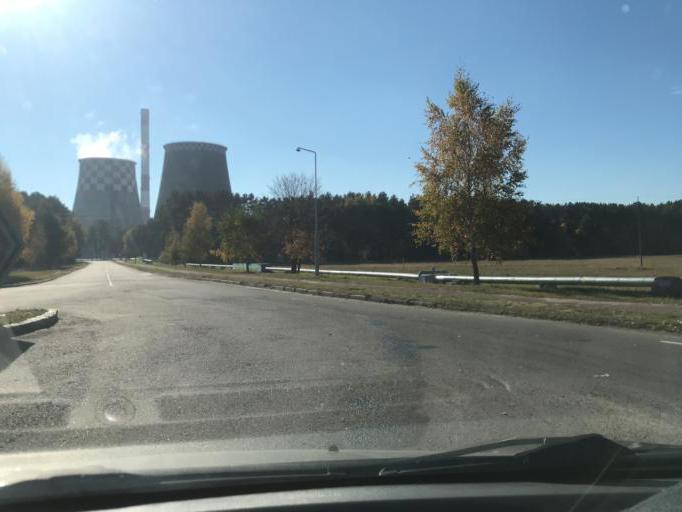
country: BY
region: Gomel
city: Kastsyukowka
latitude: 52.4558
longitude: 30.8203
